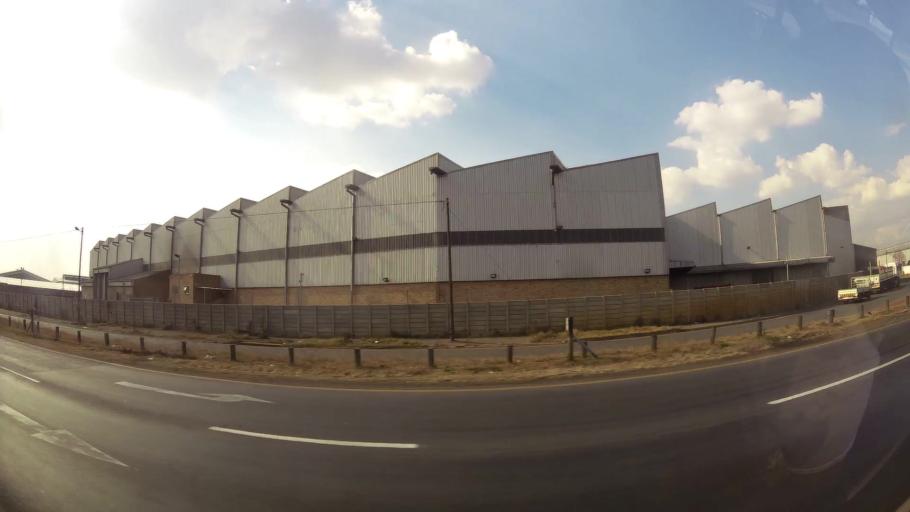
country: ZA
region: Gauteng
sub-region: Ekurhuleni Metropolitan Municipality
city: Germiston
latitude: -26.2970
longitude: 28.1772
